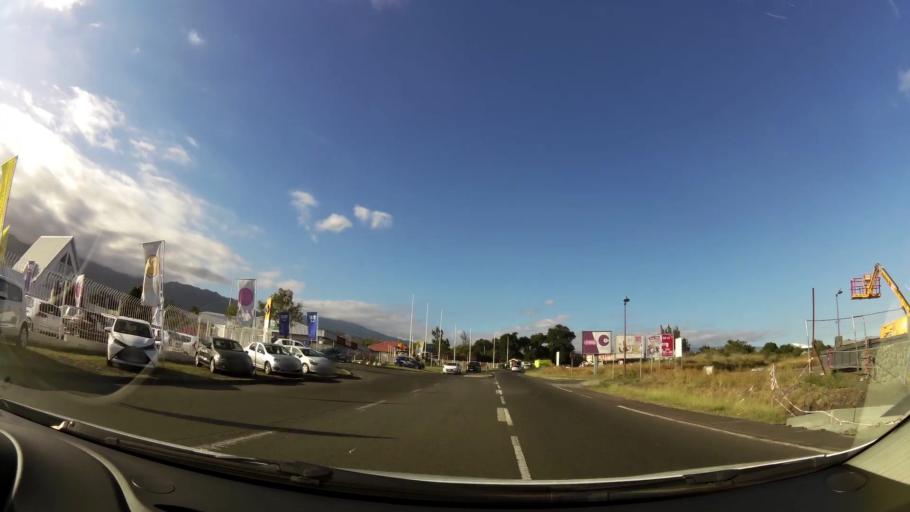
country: RE
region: Reunion
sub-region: Reunion
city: Saint-Louis
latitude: -21.2828
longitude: 55.4004
